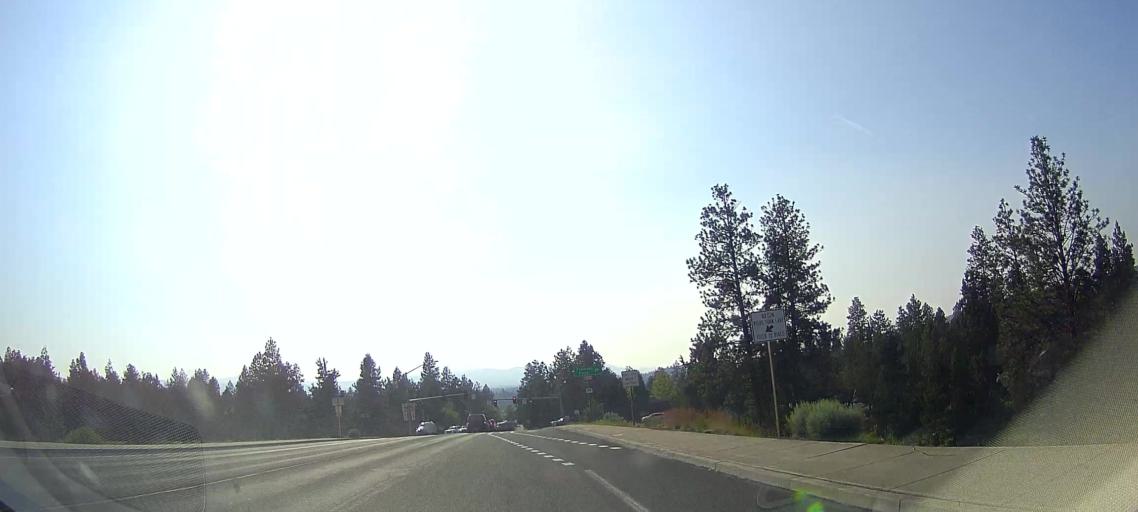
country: US
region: Oregon
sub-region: Deschutes County
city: Bend
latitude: 44.0388
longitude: -121.3086
